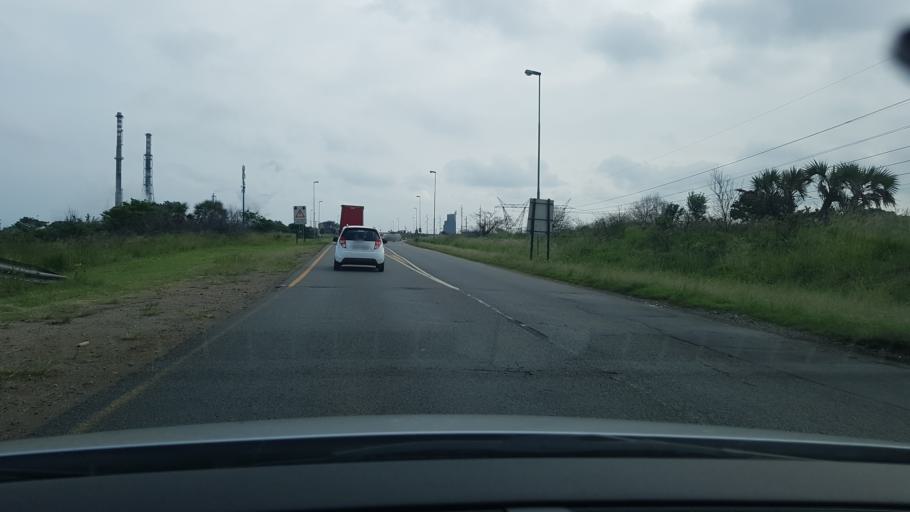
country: ZA
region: KwaZulu-Natal
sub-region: uThungulu District Municipality
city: Richards Bay
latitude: -28.7661
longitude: 32.0369
